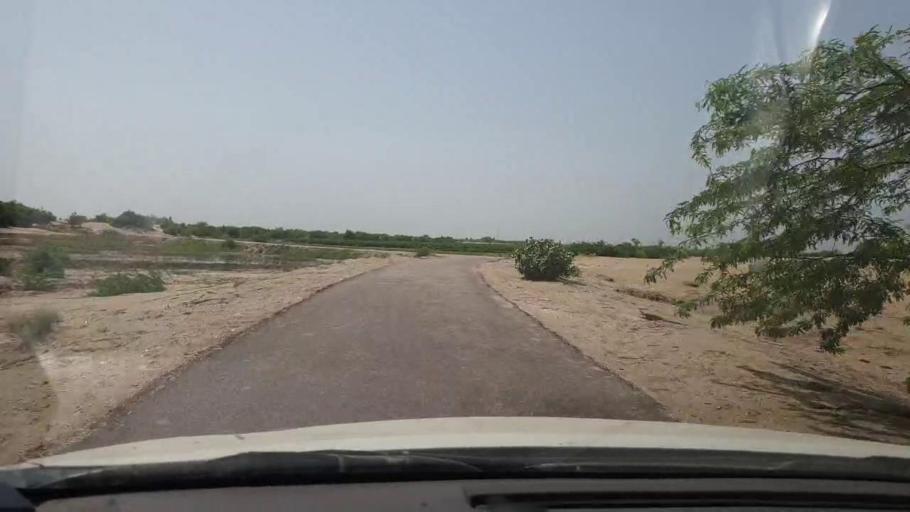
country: PK
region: Sindh
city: Rohri
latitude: 27.5205
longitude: 69.0727
